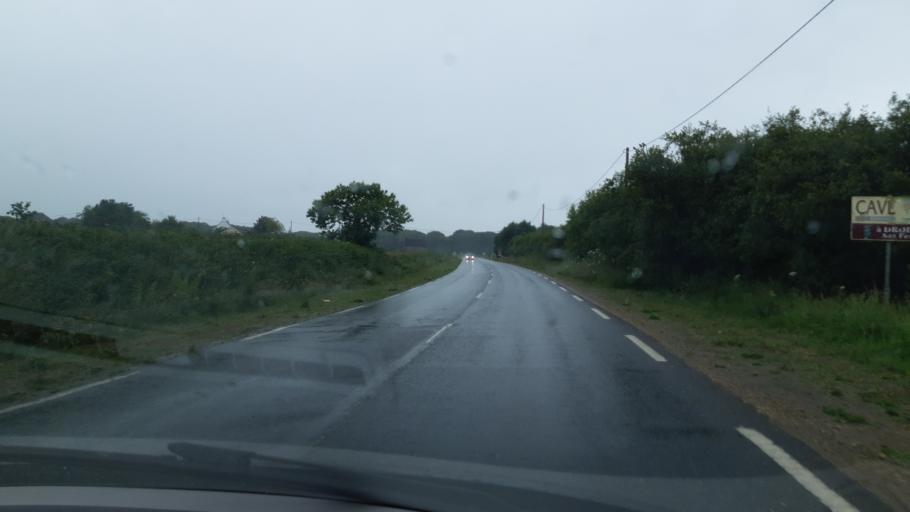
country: FR
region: Brittany
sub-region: Departement du Finistere
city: Plouvorn
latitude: 48.5958
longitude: -4.0522
